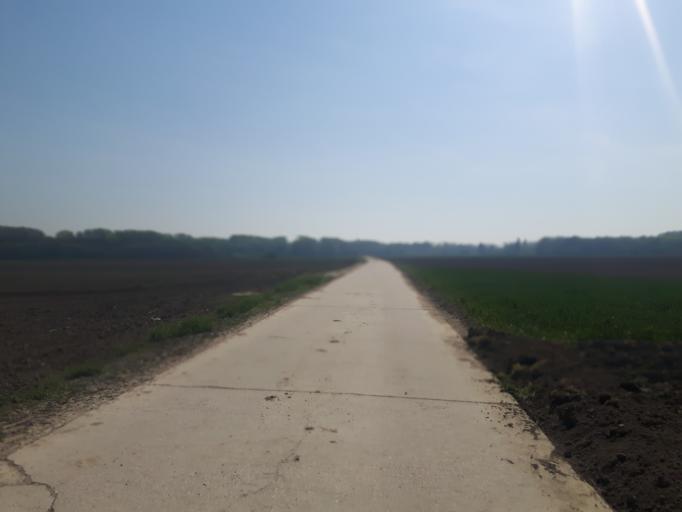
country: DE
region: Rheinland-Pfalz
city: Waldsee
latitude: 49.4028
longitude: 8.4592
